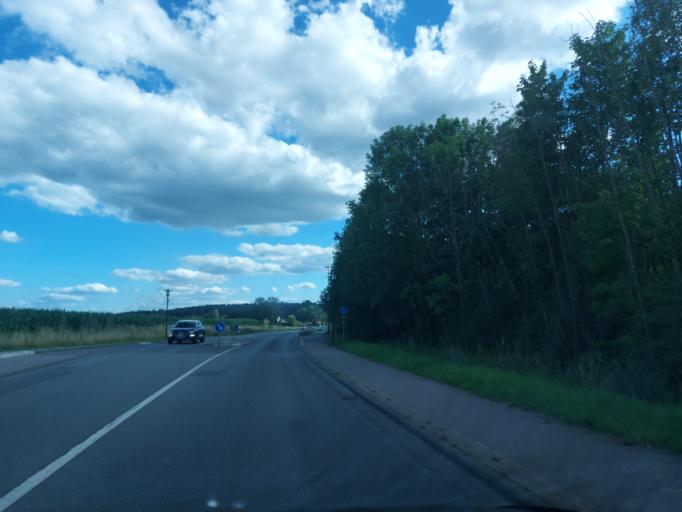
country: DE
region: Lower Saxony
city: Hilter
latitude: 52.1305
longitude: 8.1527
